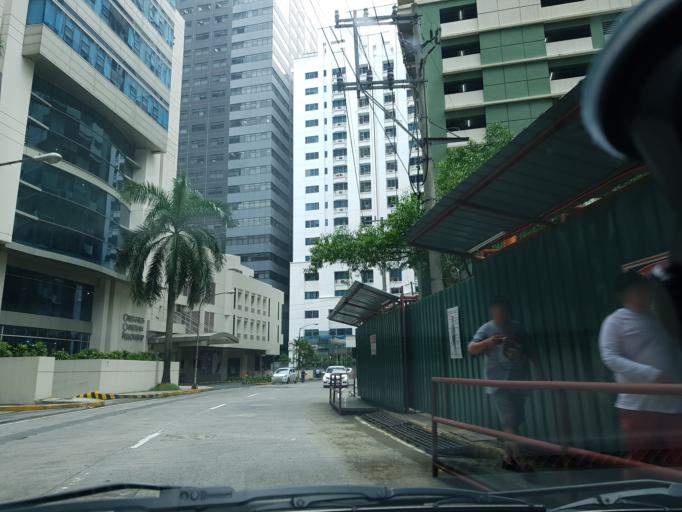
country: PH
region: Metro Manila
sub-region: Pasig
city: Pasig City
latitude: 14.5882
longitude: 121.0610
